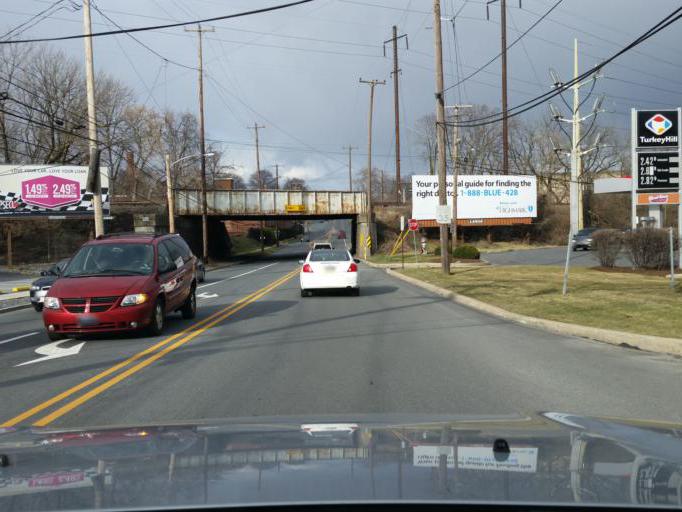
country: US
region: Pennsylvania
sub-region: Lancaster County
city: Lancaster
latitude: 40.0515
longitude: -76.2900
